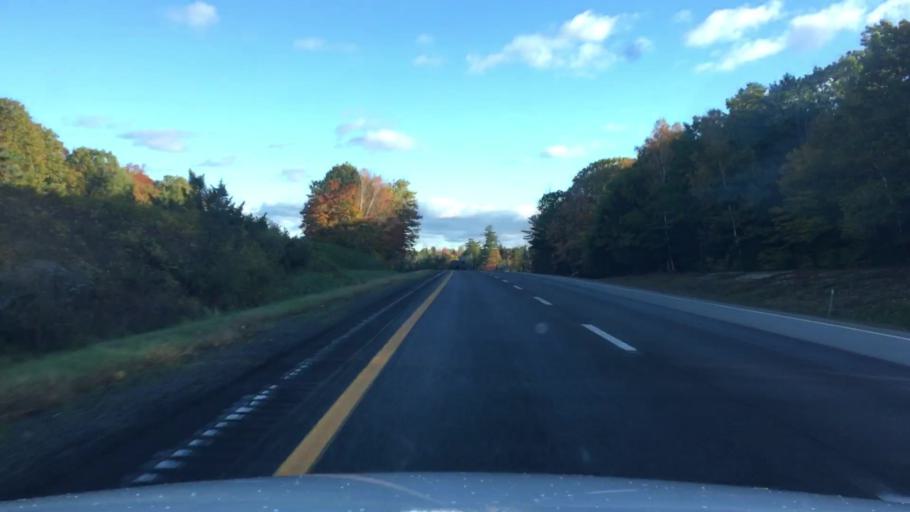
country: US
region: Maine
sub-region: Penobscot County
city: Orono
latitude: 44.8758
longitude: -68.7000
